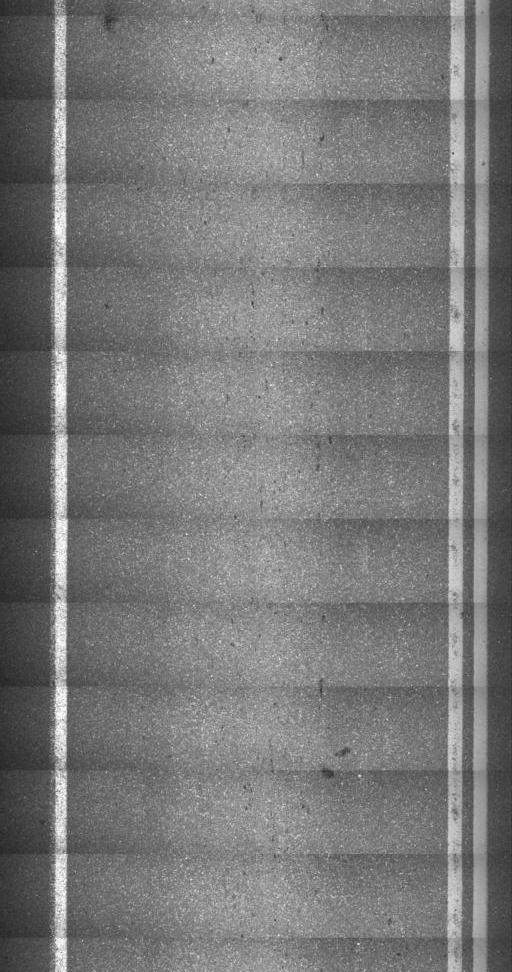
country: US
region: New Hampshire
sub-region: Cheshire County
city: Westmoreland
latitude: 42.9696
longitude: -72.5224
